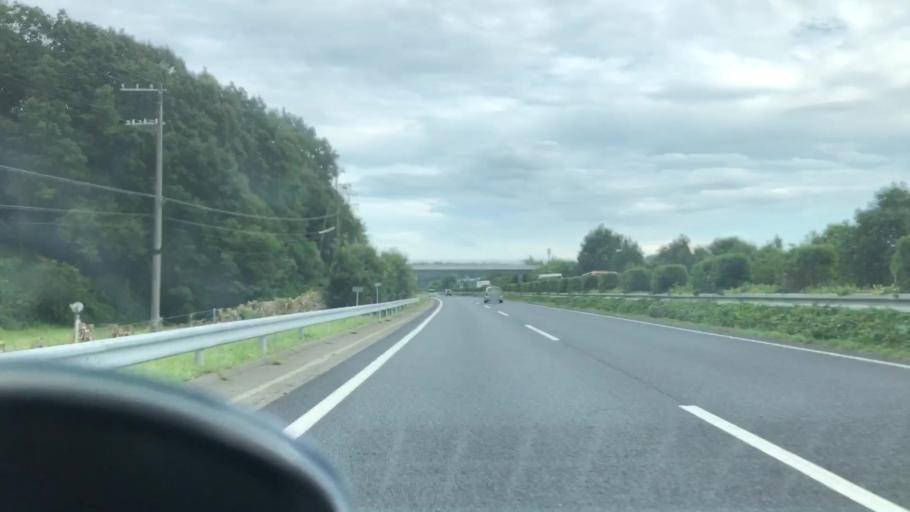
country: JP
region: Hyogo
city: Yashiro
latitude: 34.9230
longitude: 134.9908
